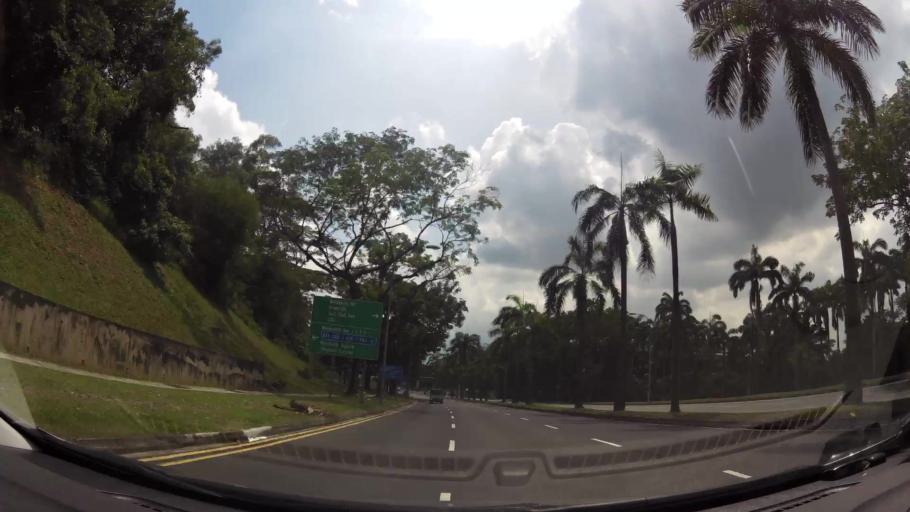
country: MY
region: Johor
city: Johor Bahru
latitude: 1.4283
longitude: 103.7623
